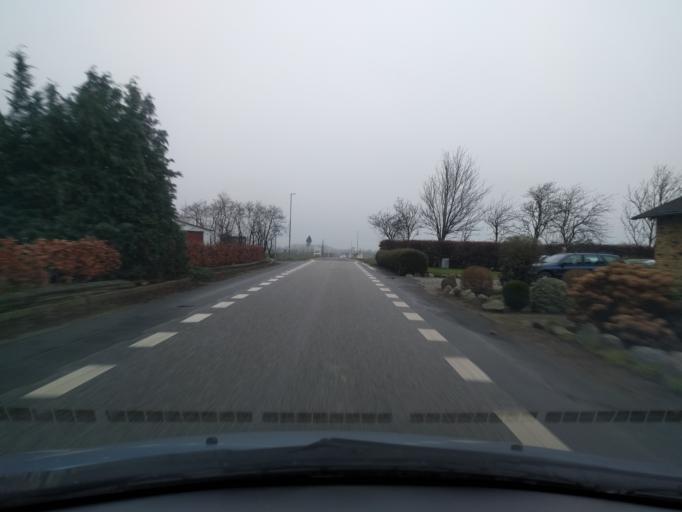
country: DK
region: South Denmark
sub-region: Odense Kommune
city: Bullerup
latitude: 55.3958
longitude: 10.5133
